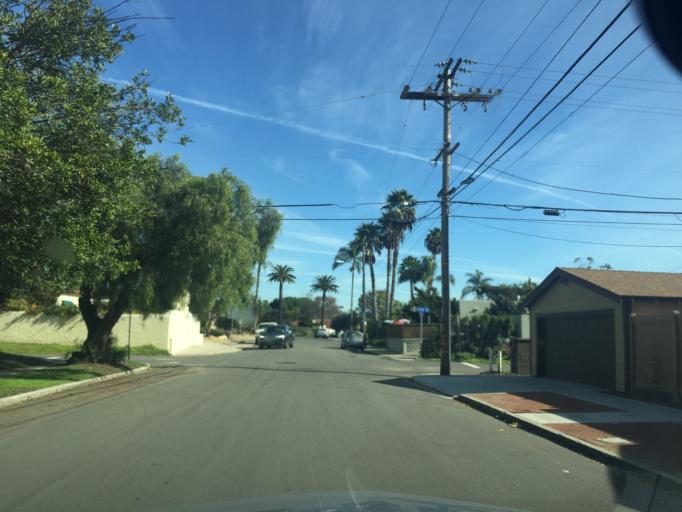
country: US
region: California
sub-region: San Diego County
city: San Diego
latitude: 32.7650
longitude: -117.1051
